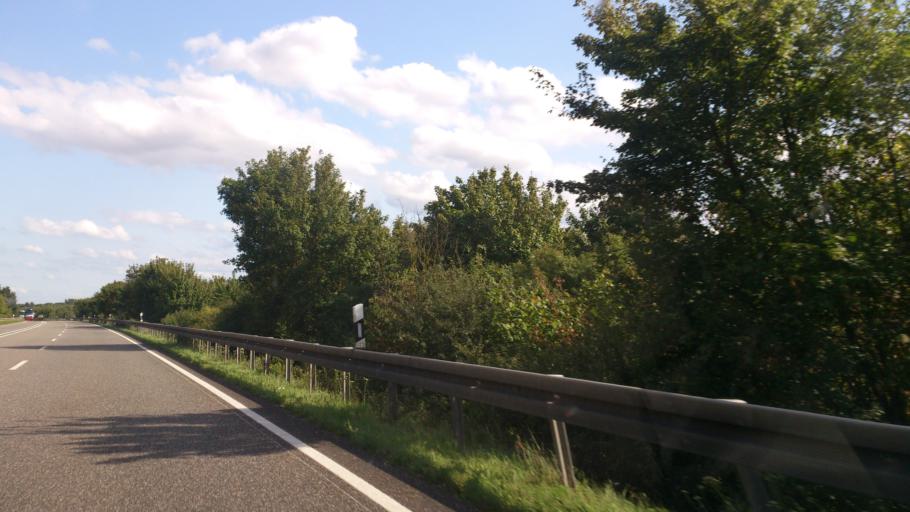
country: DE
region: North Rhine-Westphalia
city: Zulpich
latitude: 50.6826
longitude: 6.7136
